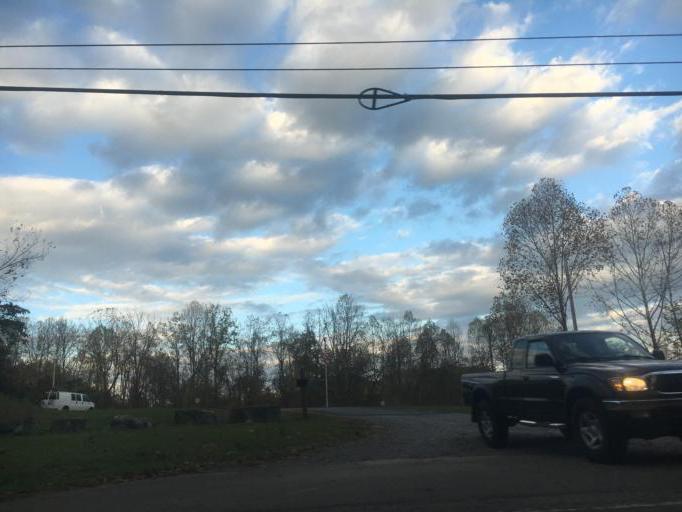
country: US
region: Tennessee
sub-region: Sullivan County
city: Colonial Heights
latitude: 36.4714
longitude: -82.4849
